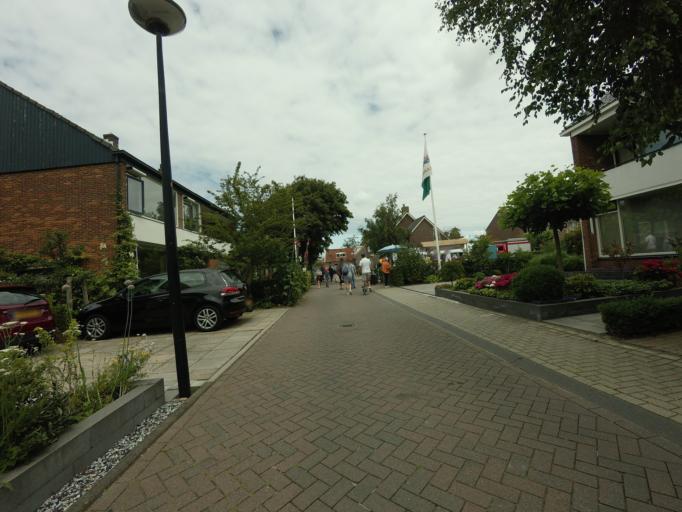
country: NL
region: South Holland
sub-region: Gemeente Teylingen
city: Sassenheim
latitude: 52.2135
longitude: 4.5580
